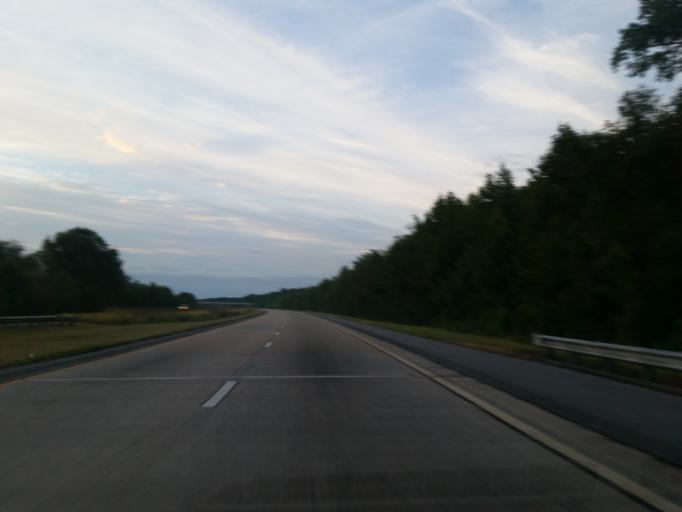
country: US
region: Delaware
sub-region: Kent County
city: Cheswold
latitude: 39.2334
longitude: -75.5784
